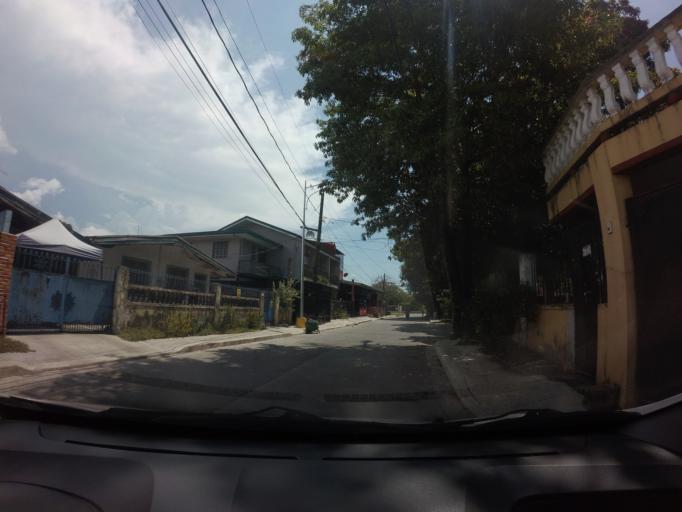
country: PH
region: Calabarzon
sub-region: Province of Rizal
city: Las Pinas
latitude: 14.4228
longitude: 120.9876
